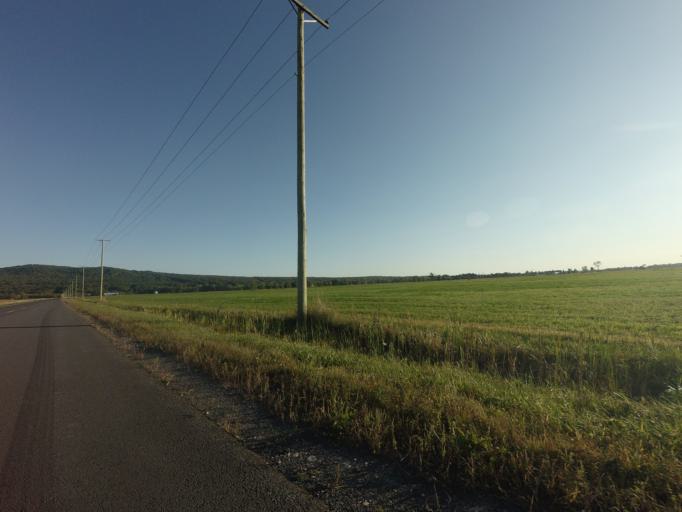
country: CA
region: Quebec
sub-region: Monteregie
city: Rigaud
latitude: 45.4800
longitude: -74.3435
